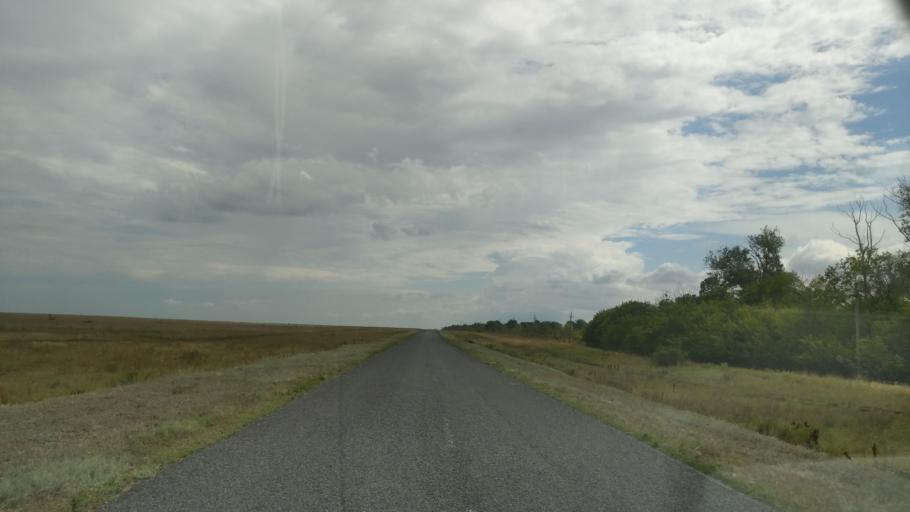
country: KZ
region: Pavlodar
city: Pavlodar
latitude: 52.6440
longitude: 77.0536
